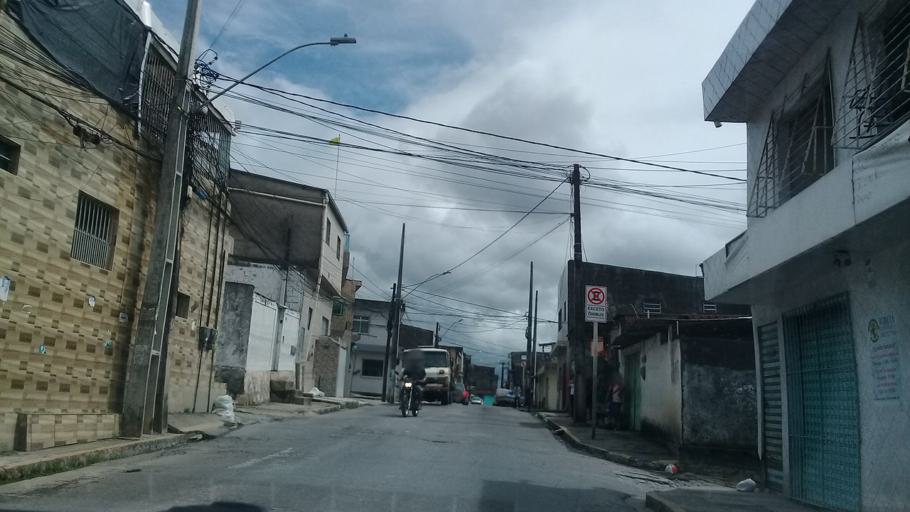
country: BR
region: Pernambuco
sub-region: Jaboatao Dos Guararapes
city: Jaboatao dos Guararapes
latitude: -8.1140
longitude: -34.9538
